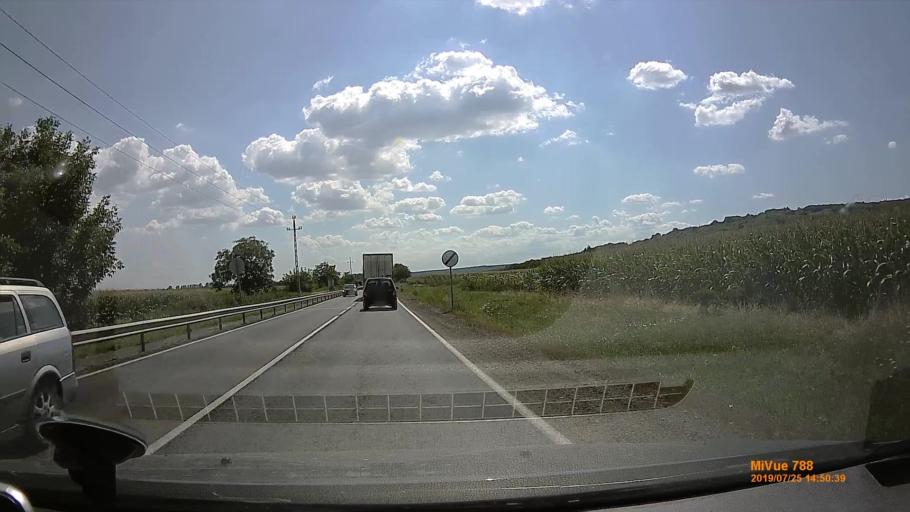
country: HU
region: Borsod-Abauj-Zemplen
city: Aszalo
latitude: 48.2216
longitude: 20.9507
